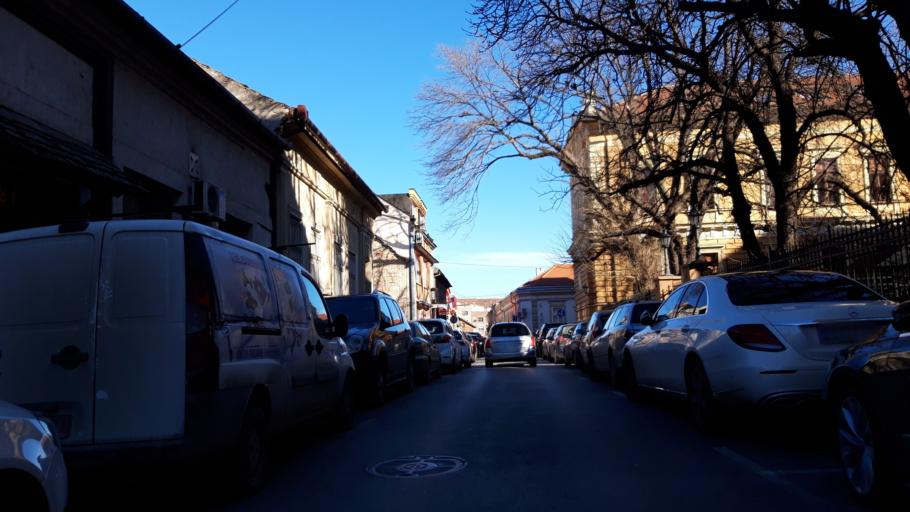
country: RS
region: Autonomna Pokrajina Vojvodina
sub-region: Juznobacki Okrug
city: Novi Sad
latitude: 45.2582
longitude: 19.8470
